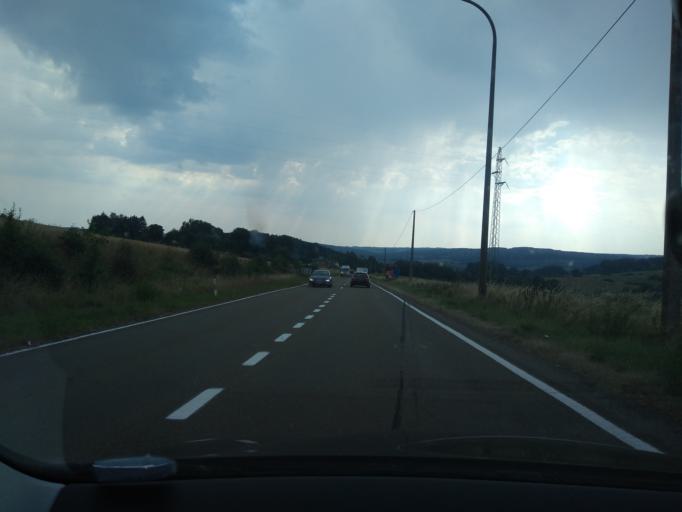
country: BE
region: Wallonia
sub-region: Province du Luxembourg
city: Sainte-Ode
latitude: 50.0441
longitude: 5.5614
